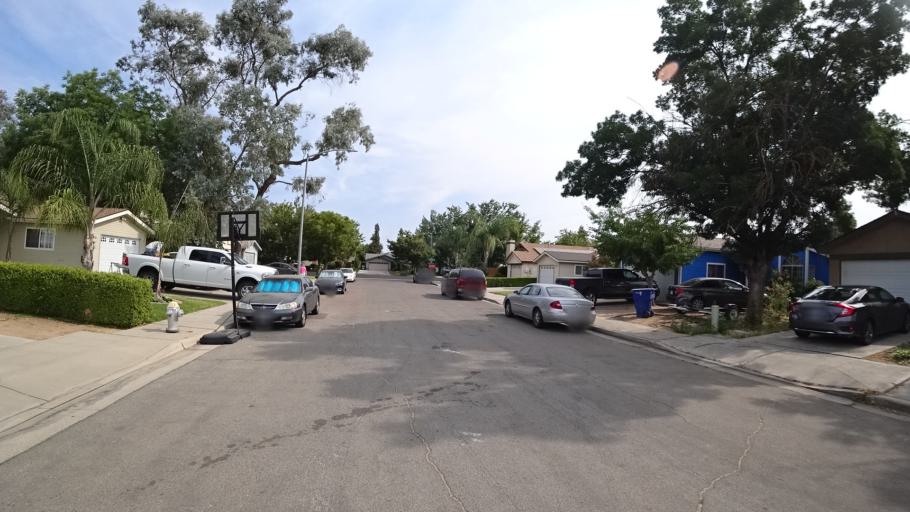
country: US
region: California
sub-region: Fresno County
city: West Park
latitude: 36.7713
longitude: -119.8740
